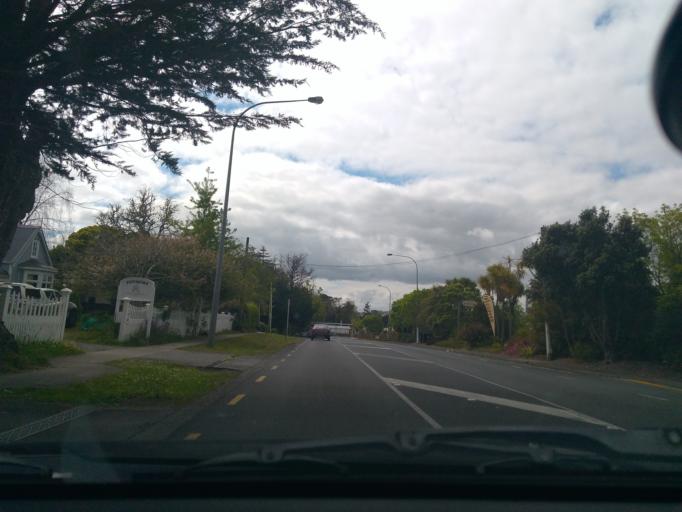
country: NZ
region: Auckland
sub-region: Auckland
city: Rosebank
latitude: -36.8657
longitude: 174.5759
